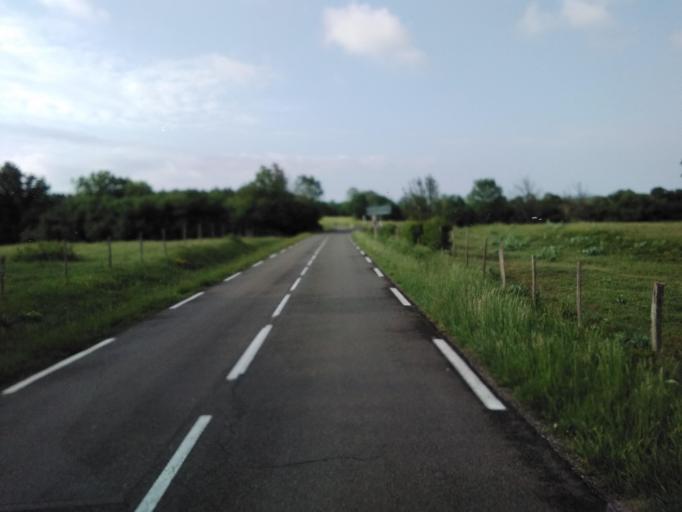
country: FR
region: Franche-Comte
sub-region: Departement du Jura
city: Arbois
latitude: 46.8276
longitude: 5.8220
